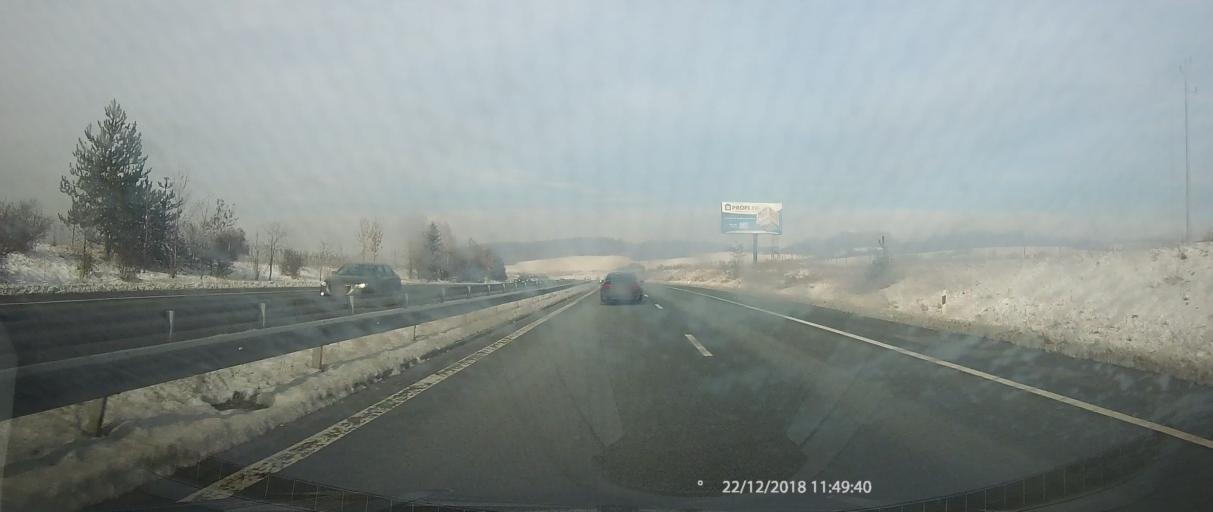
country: BG
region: Pernik
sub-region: Obshtina Pernik
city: Pernik
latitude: 42.5491
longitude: 23.1258
